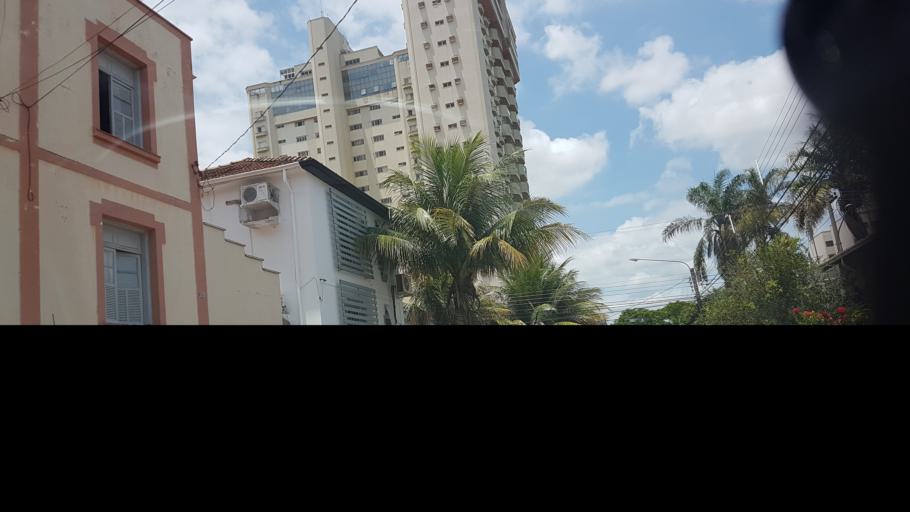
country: BR
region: Sao Paulo
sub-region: Piracicaba
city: Piracicaba
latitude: -22.7223
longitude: -47.6525
